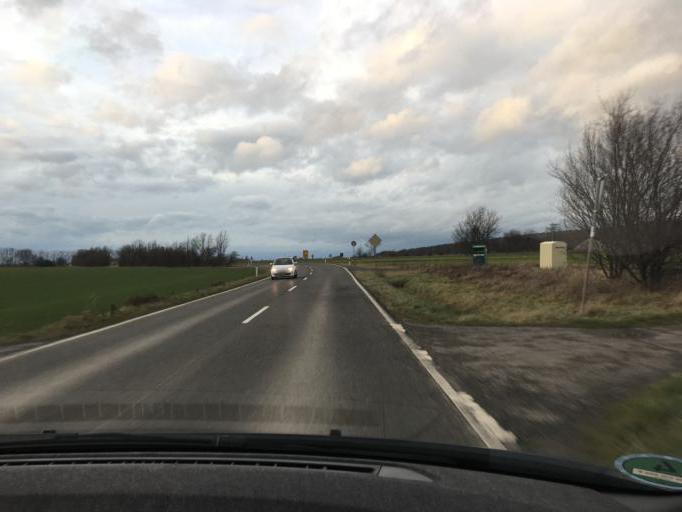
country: DE
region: North Rhine-Westphalia
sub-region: Regierungsbezirk Koln
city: Bad Munstereifel
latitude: 50.6081
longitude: 6.7393
